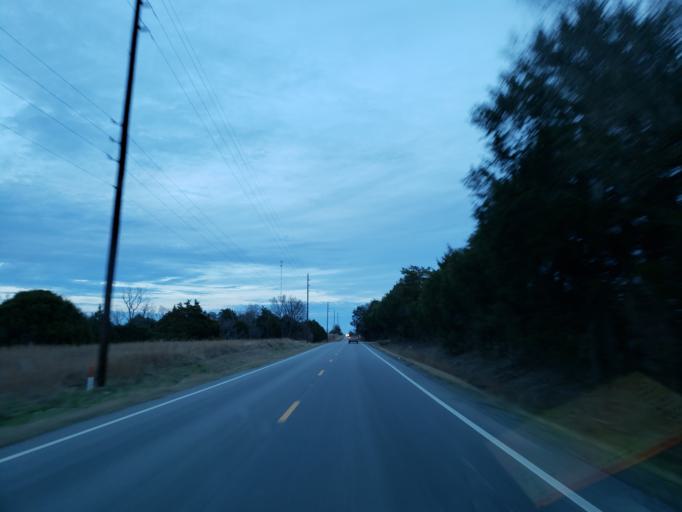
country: US
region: Alabama
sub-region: Sumter County
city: Livingston
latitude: 32.8062
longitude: -88.3014
